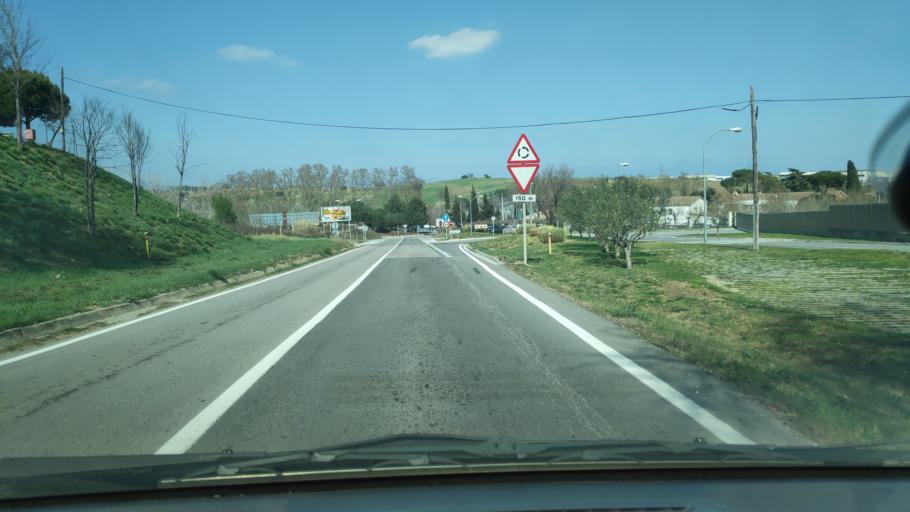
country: ES
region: Catalonia
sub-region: Provincia de Barcelona
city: Polinya
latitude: 41.5314
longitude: 2.1529
